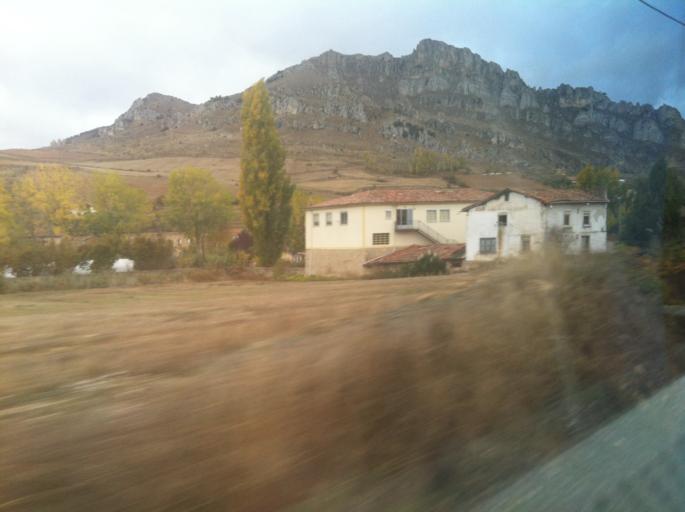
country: ES
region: Castille and Leon
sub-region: Provincia de Burgos
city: Pancorbo
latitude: 42.6288
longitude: -3.1135
